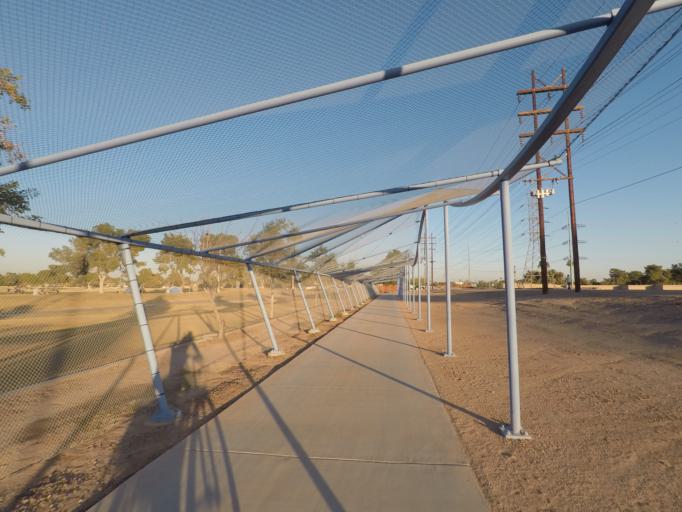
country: US
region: Arizona
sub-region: Maricopa County
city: Guadalupe
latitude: 33.3570
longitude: -111.9345
